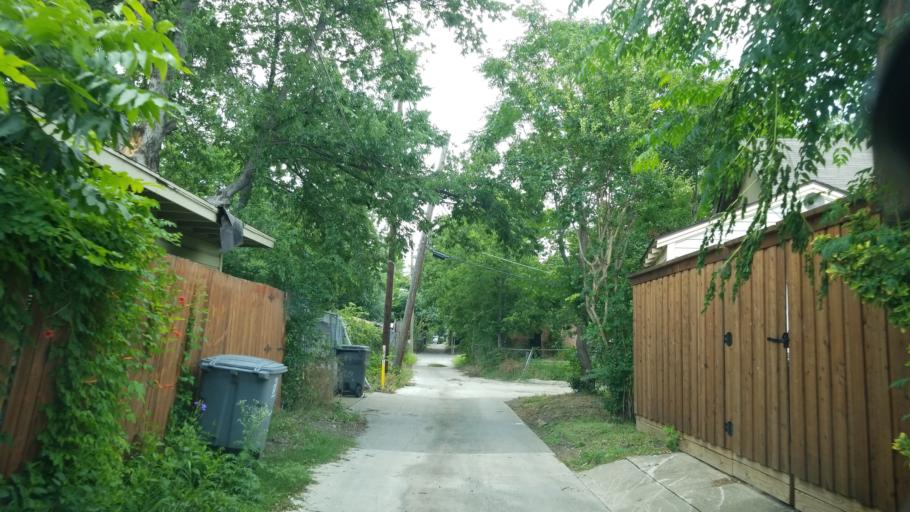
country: US
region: Texas
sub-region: Dallas County
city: Farmers Branch
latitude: 32.8735
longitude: -96.8642
